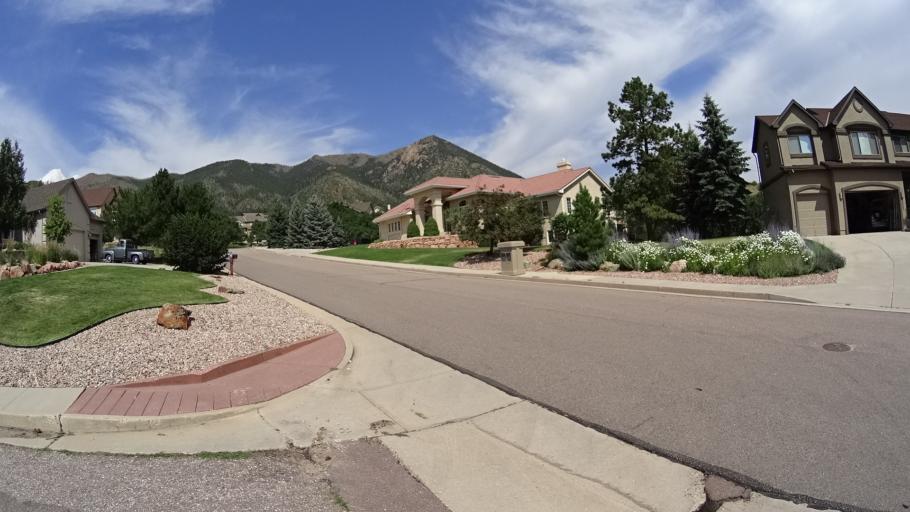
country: US
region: Colorado
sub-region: El Paso County
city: Air Force Academy
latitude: 38.9473
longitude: -104.8803
